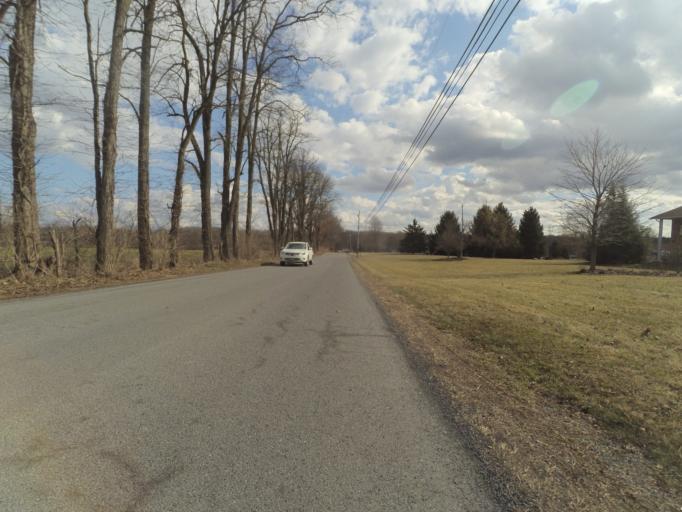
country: US
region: Pennsylvania
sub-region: Centre County
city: Stormstown
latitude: 40.8017
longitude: -77.9908
